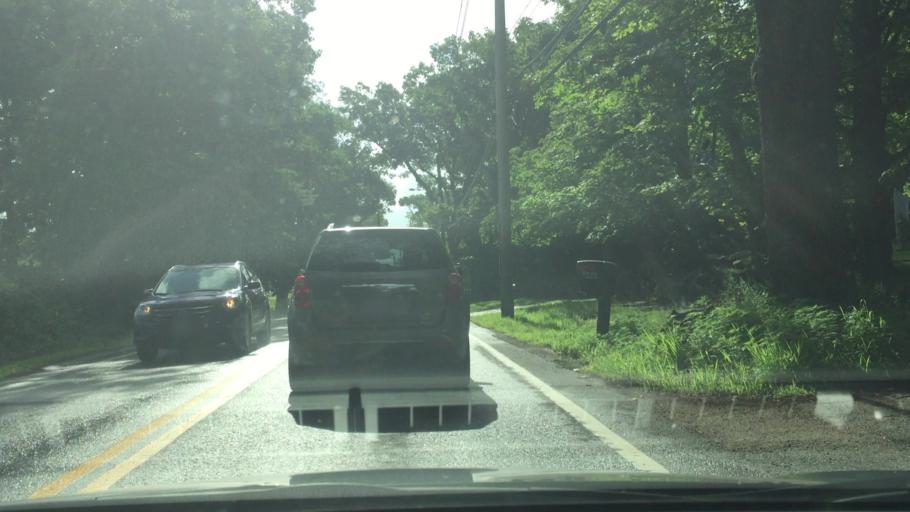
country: US
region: Massachusetts
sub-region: Middlesex County
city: Acton
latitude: 42.4752
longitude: -71.4581
